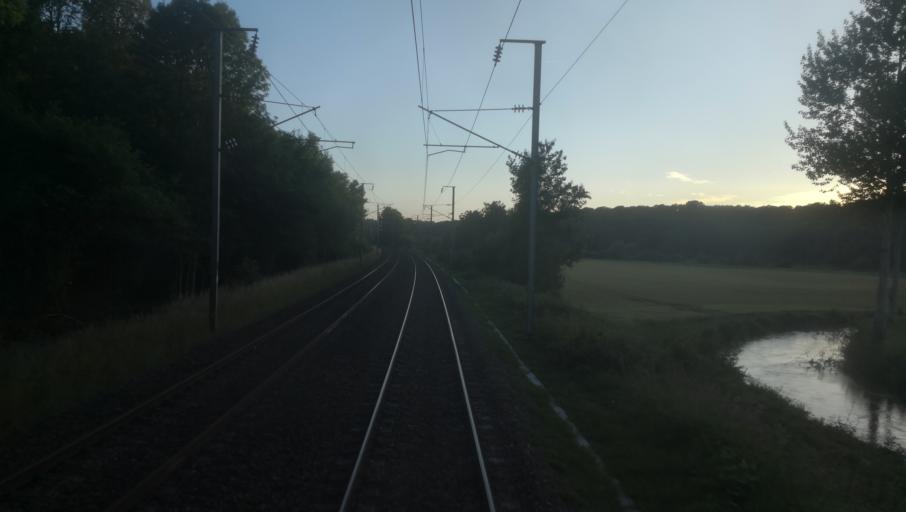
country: FR
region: Haute-Normandie
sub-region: Departement de l'Eure
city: Conches-en-Ouche
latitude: 48.9769
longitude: 0.9949
